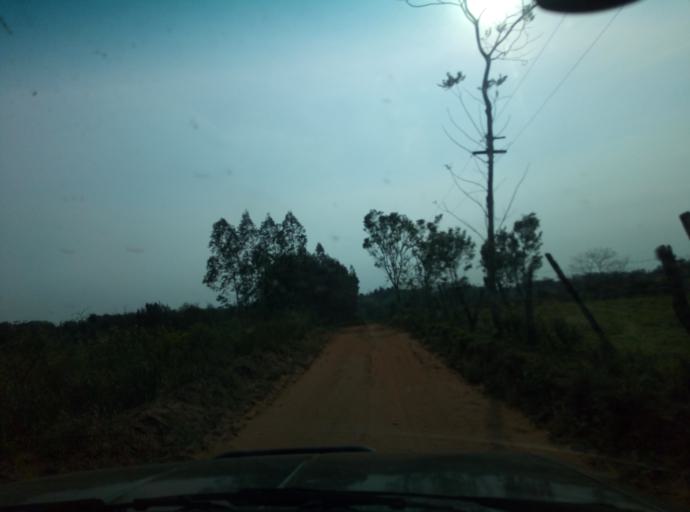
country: PY
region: Caaguazu
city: San Joaquin
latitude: -25.1547
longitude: -56.1057
